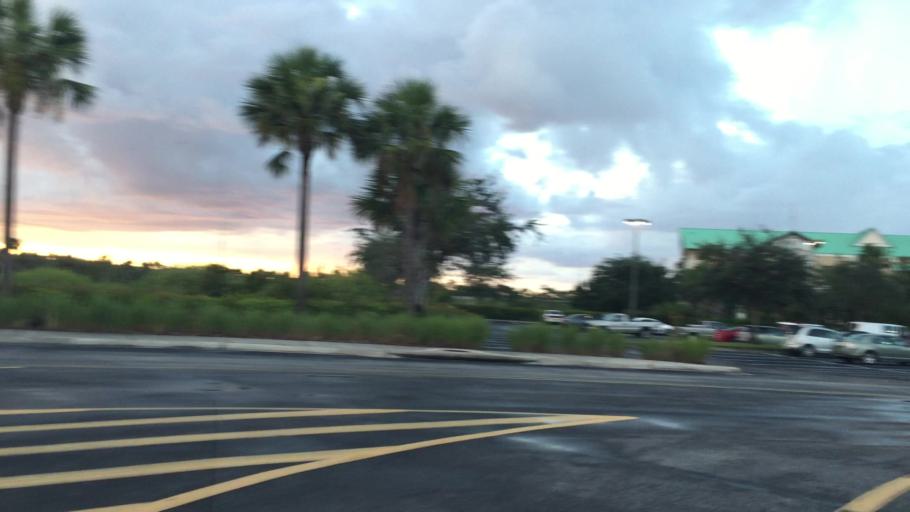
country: US
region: Florida
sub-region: Lee County
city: Three Oaks
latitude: 26.4860
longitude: -81.7916
